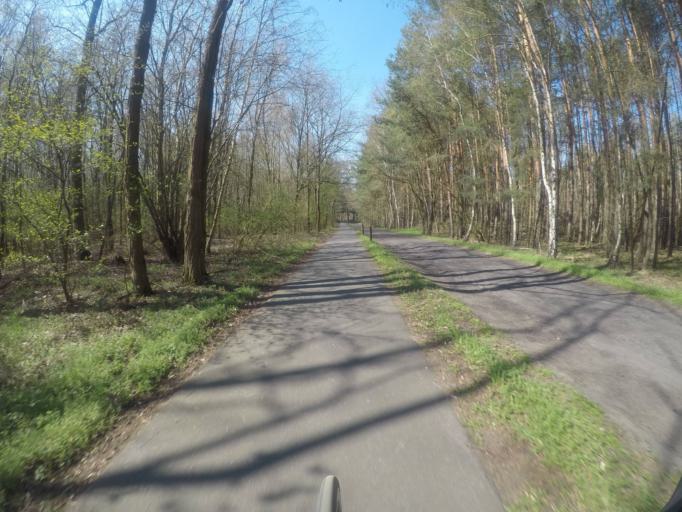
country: DE
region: Brandenburg
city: Nauen
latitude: 52.6591
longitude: 12.9439
